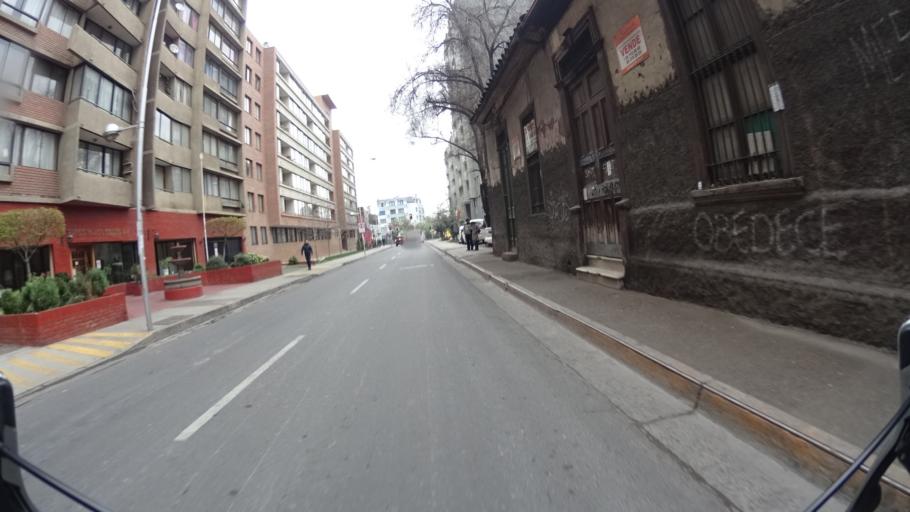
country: CL
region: Santiago Metropolitan
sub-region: Provincia de Santiago
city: Santiago
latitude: -33.4504
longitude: -70.6552
